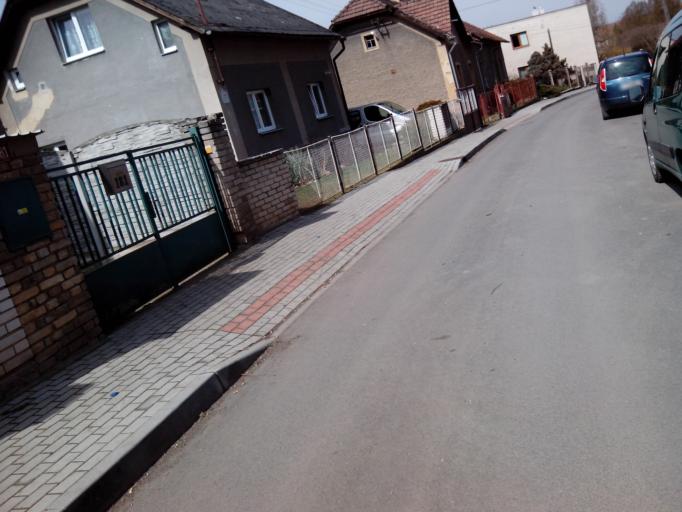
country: CZ
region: Central Bohemia
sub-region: Okres Beroun
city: Beroun
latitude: 49.9462
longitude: 14.1007
